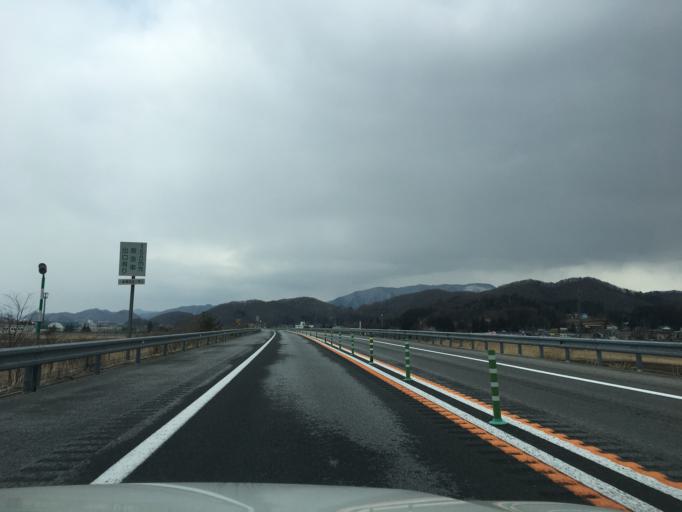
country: JP
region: Aomori
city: Aomori Shi
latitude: 40.8042
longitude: 140.7945
